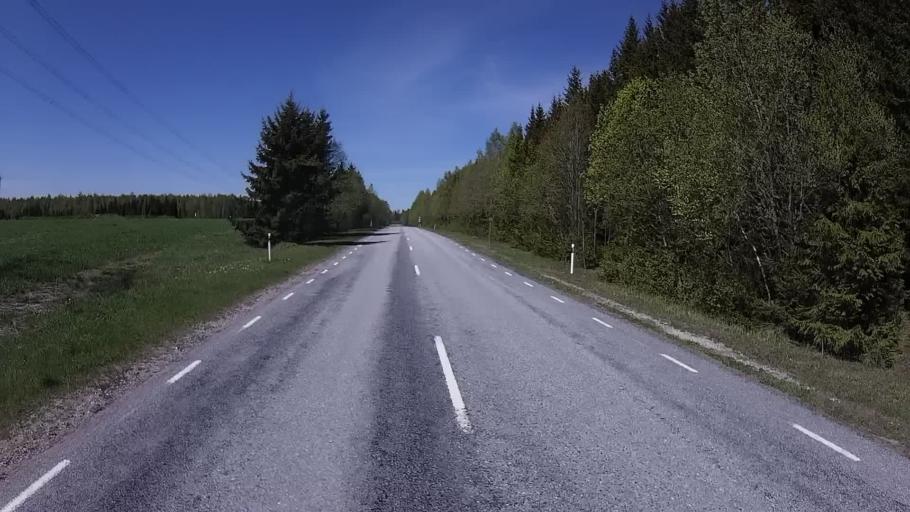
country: EE
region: Raplamaa
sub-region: Kehtna vald
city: Kehtna
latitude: 59.0410
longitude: 25.0354
